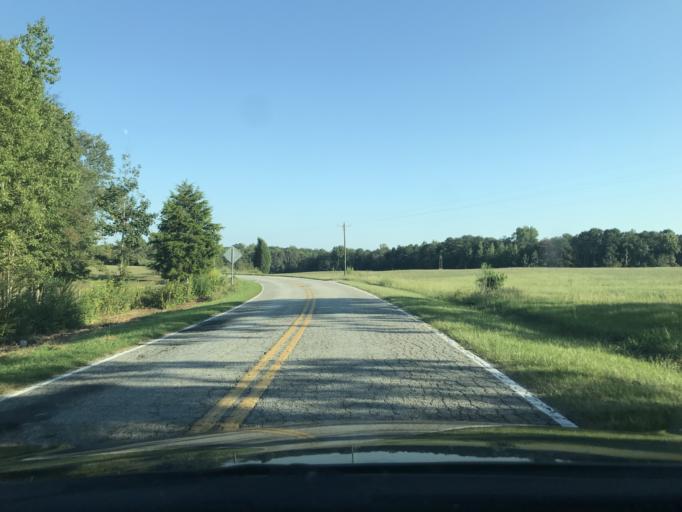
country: US
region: South Carolina
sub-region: Spartanburg County
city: Mayo
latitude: 35.1097
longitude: -81.7845
